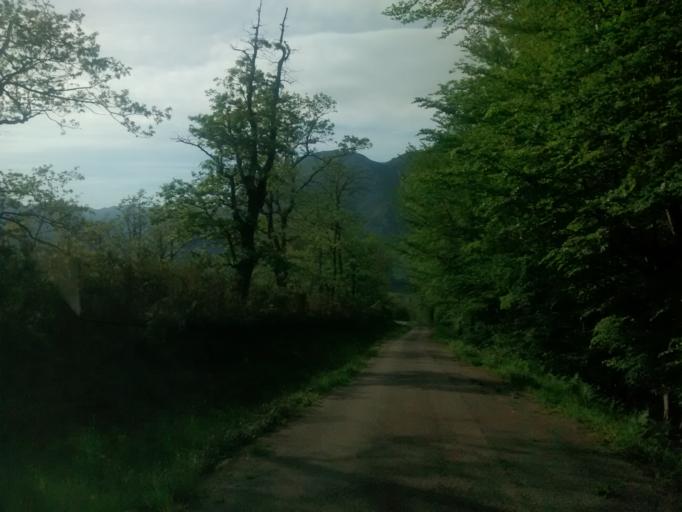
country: ES
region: Cantabria
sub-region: Provincia de Cantabria
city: Tresviso
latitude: 43.2420
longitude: -4.5738
